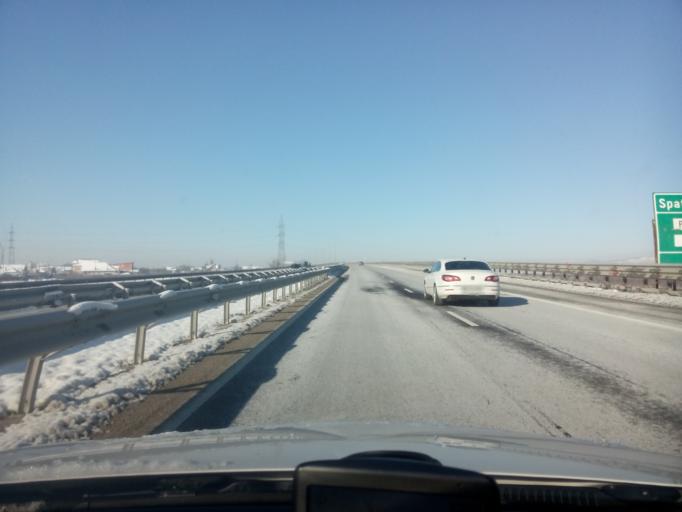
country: RO
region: Arges
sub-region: Oras Stefanesti
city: Golesti
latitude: 44.8244
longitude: 24.9390
